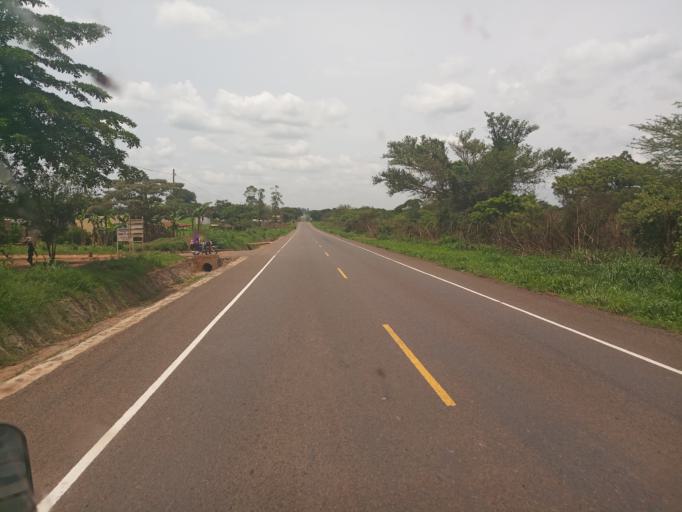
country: UG
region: Northern Region
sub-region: Oyam District
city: Oyam
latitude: 2.1744
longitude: 32.2233
